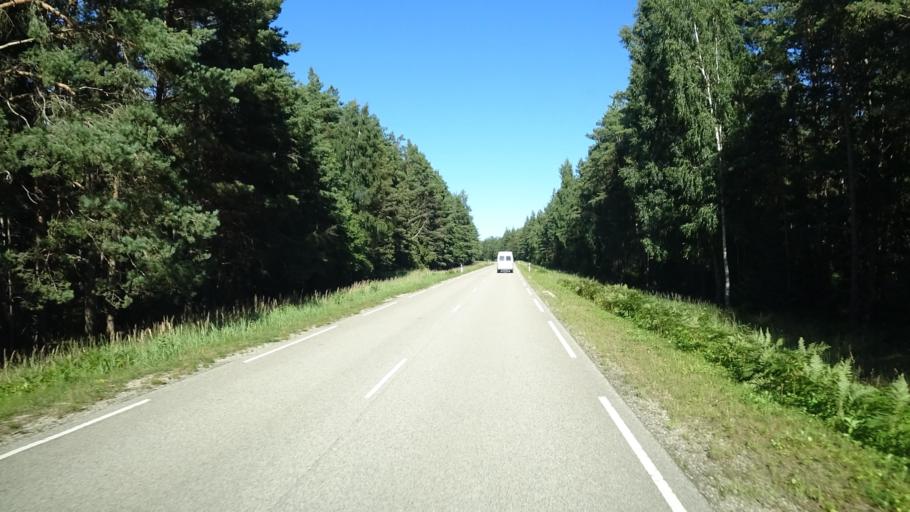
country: LV
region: Dundaga
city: Dundaga
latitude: 57.7441
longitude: 22.5552
